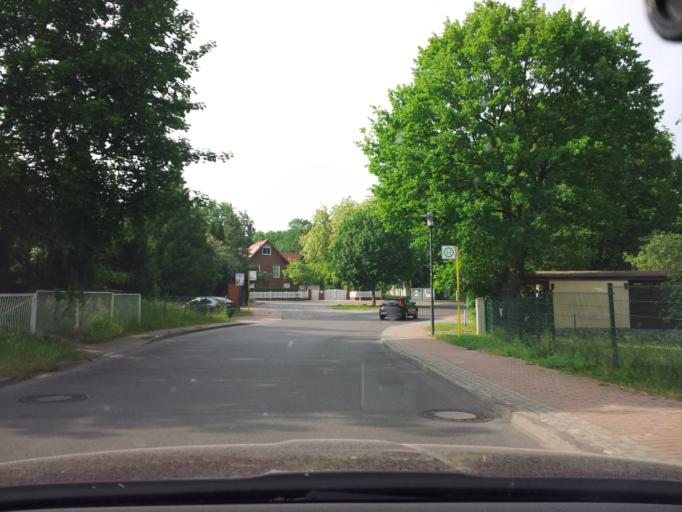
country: DE
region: Brandenburg
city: Werder
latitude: 52.3240
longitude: 12.9266
